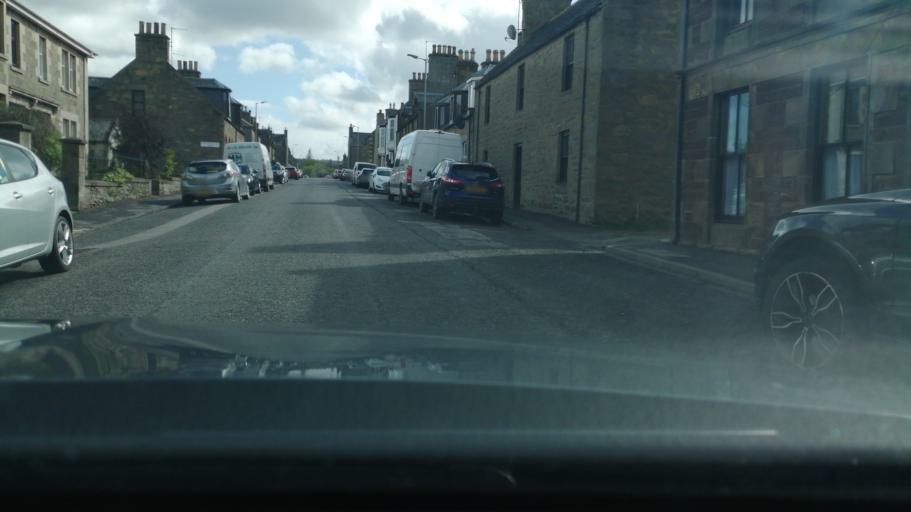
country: GB
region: Scotland
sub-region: Moray
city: Keith
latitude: 57.5400
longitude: -2.9522
